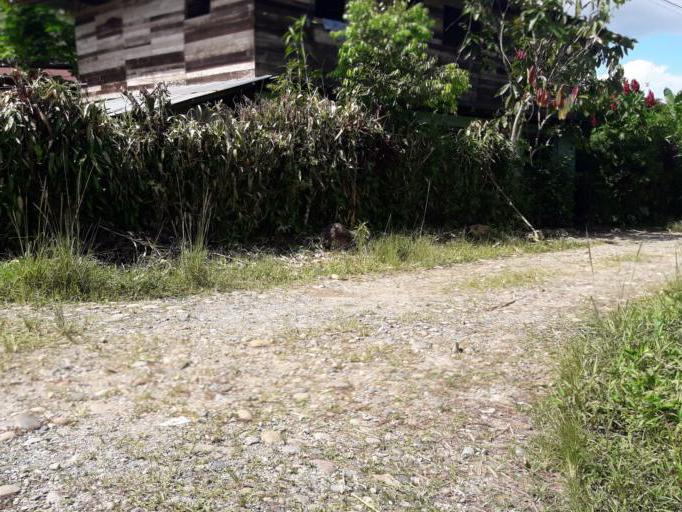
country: EC
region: Napo
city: Tena
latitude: -0.9546
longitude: -77.8240
